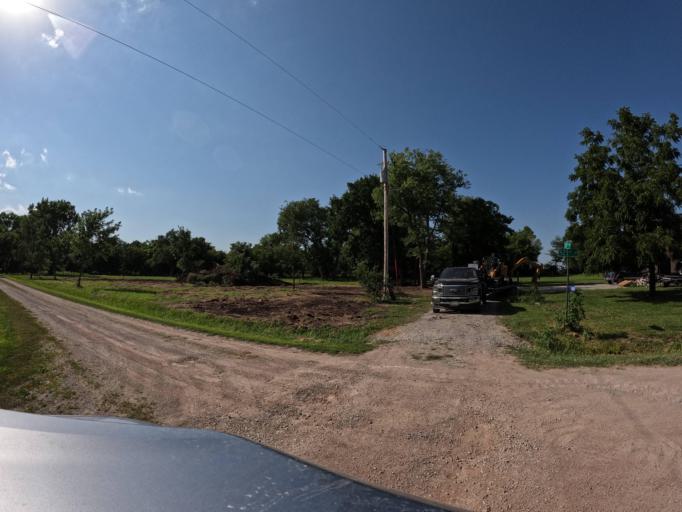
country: US
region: Iowa
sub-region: Appanoose County
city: Centerville
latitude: 40.7187
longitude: -93.0319
